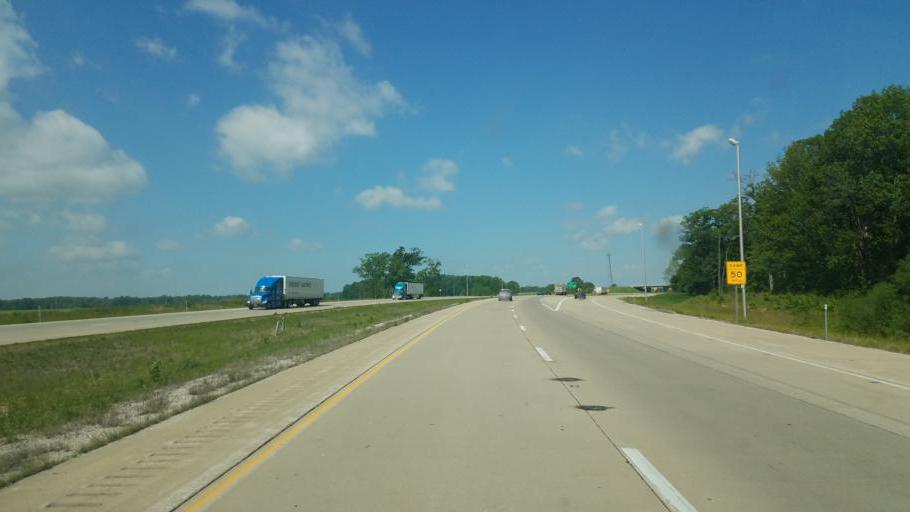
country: US
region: Indiana
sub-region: Vigo County
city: West Terre Haute
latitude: 39.4268
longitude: -87.5526
